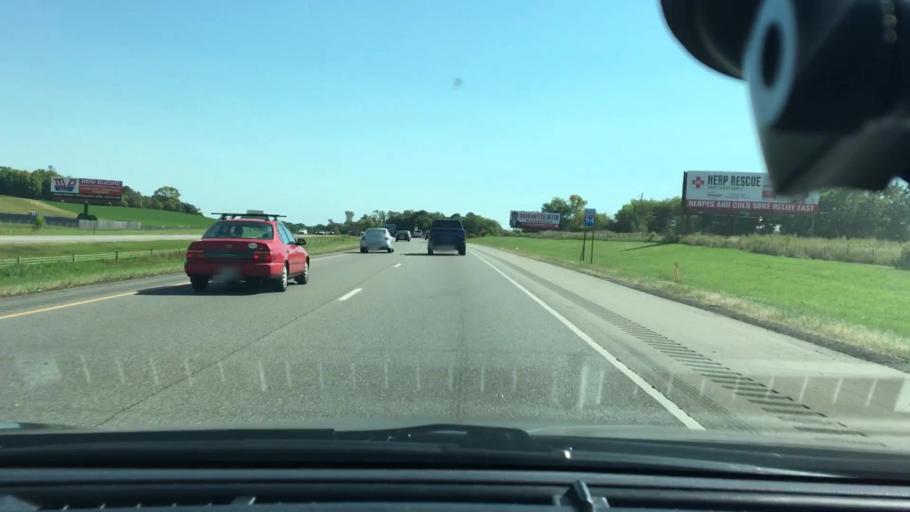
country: US
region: Minnesota
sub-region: Wright County
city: Albertville
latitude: 45.2327
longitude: -93.6423
